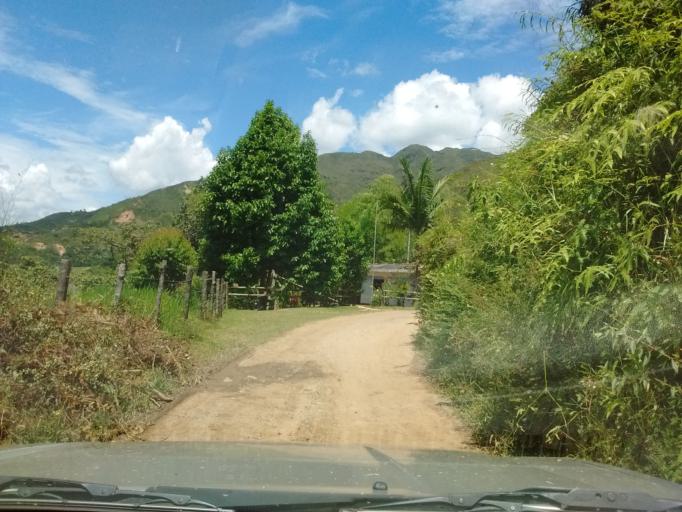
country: CO
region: Cauca
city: Villa Rica
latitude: 2.6480
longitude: -76.7689
